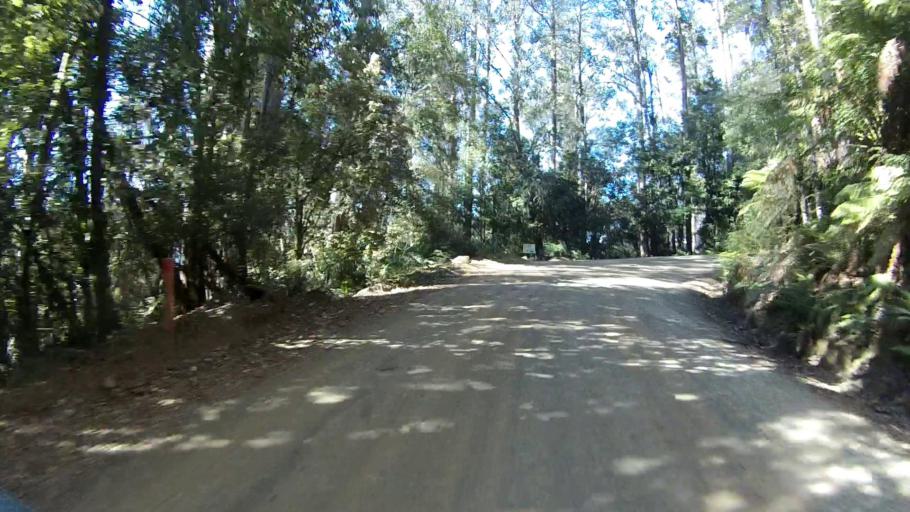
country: AU
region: Tasmania
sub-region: Derwent Valley
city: New Norfolk
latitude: -42.6788
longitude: 146.6887
